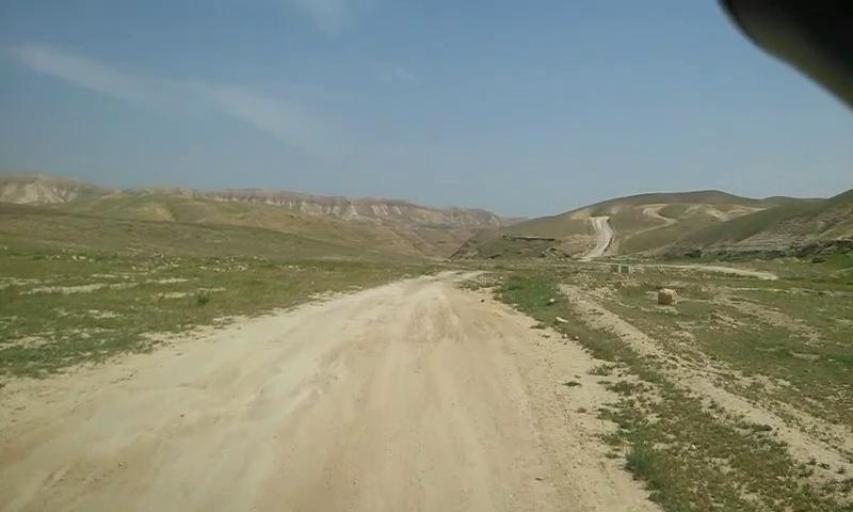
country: PS
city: `Arab ar Rashaydah
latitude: 31.5053
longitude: 35.2899
